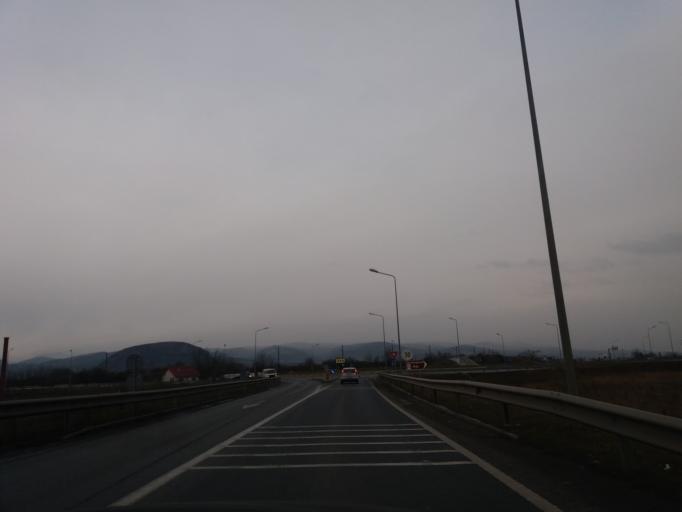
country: RO
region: Hunedoara
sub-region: Oras Simeria
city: Simeria
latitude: 45.8331
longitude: 23.0384
